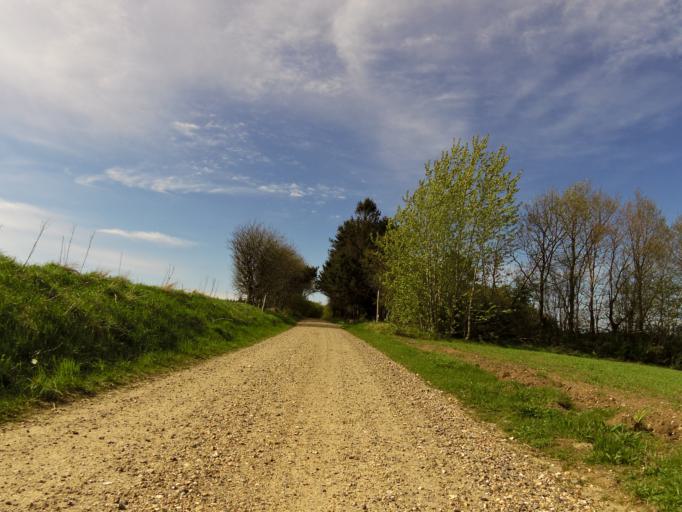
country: DK
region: Central Jutland
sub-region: Holstebro Kommune
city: Vinderup
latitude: 56.4715
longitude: 8.8830
